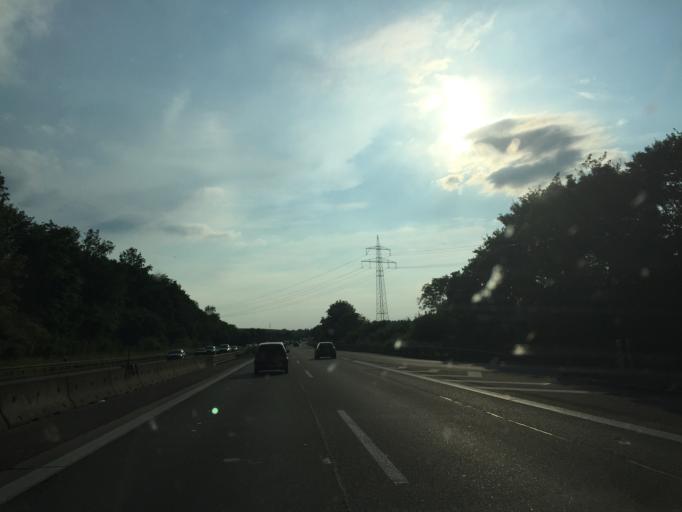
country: DE
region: Baden-Wuerttemberg
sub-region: Regierungsbezirk Stuttgart
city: Bad Wimpfen
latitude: 49.1887
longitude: 9.1643
